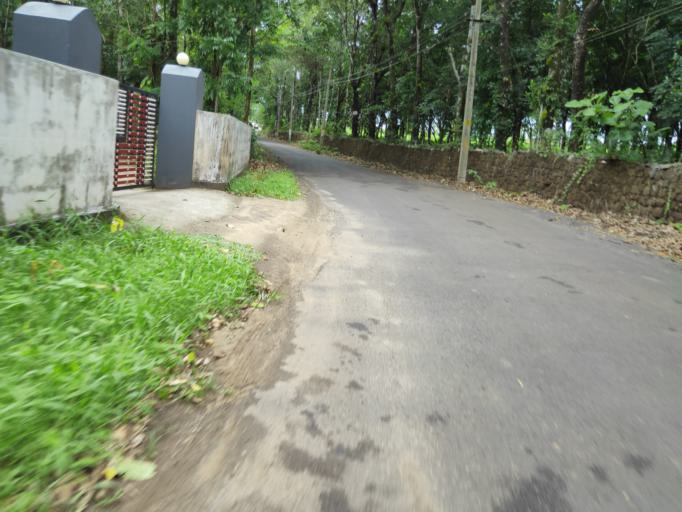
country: IN
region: Kerala
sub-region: Malappuram
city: Manjeri
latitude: 11.2390
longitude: 76.2454
